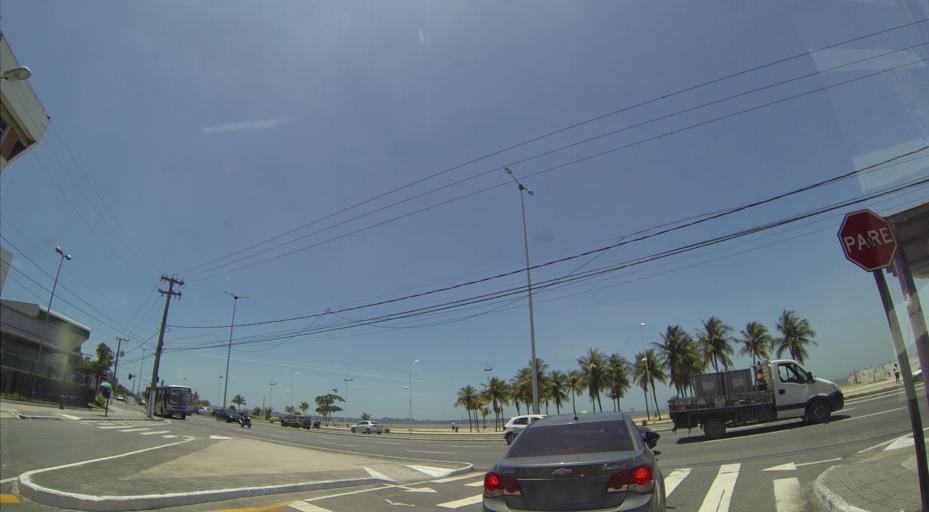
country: BR
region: Espirito Santo
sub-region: Vila Velha
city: Vila Velha
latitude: -20.2837
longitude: -40.2904
